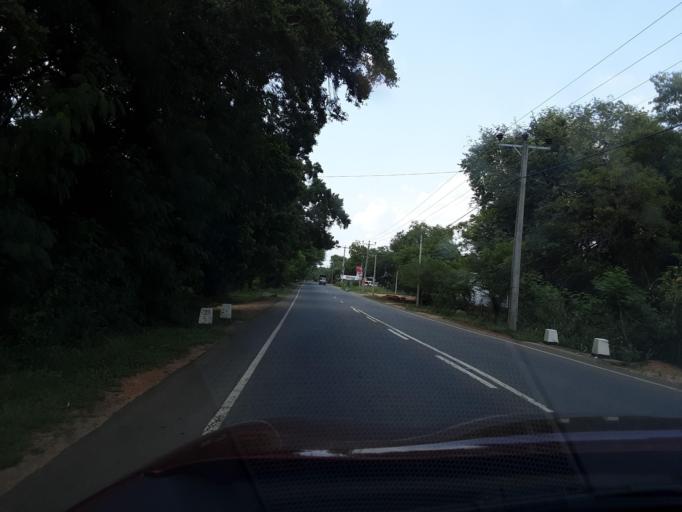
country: LK
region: Uva
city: Haputale
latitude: 6.5356
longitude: 81.1341
